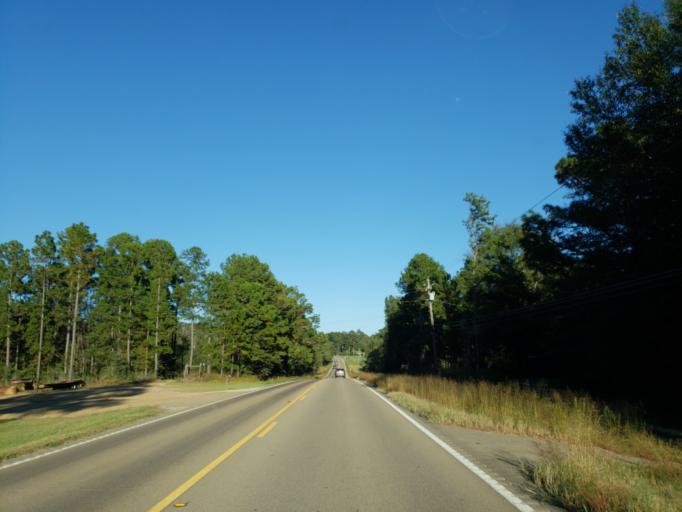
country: US
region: Mississippi
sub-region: Perry County
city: Richton
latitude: 31.3667
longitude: -88.8796
